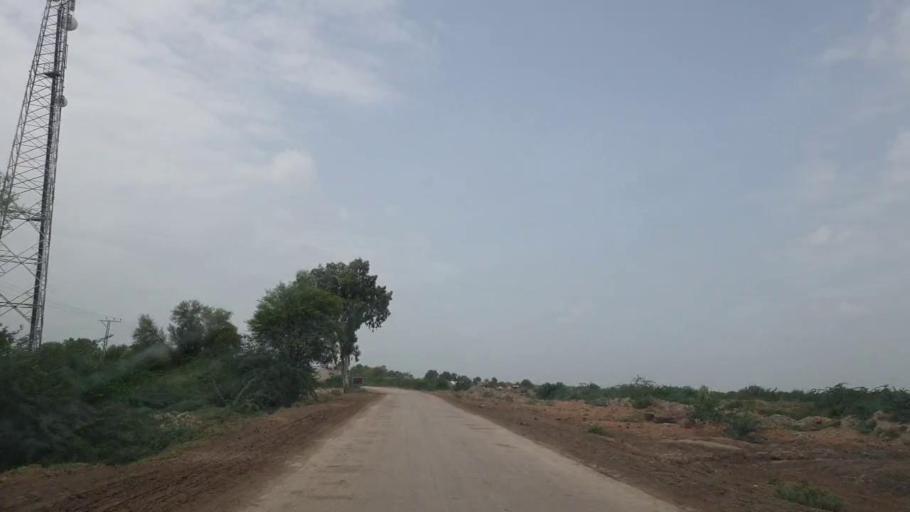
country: PK
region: Sindh
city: Tando Bago
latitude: 24.9255
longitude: 69.1091
